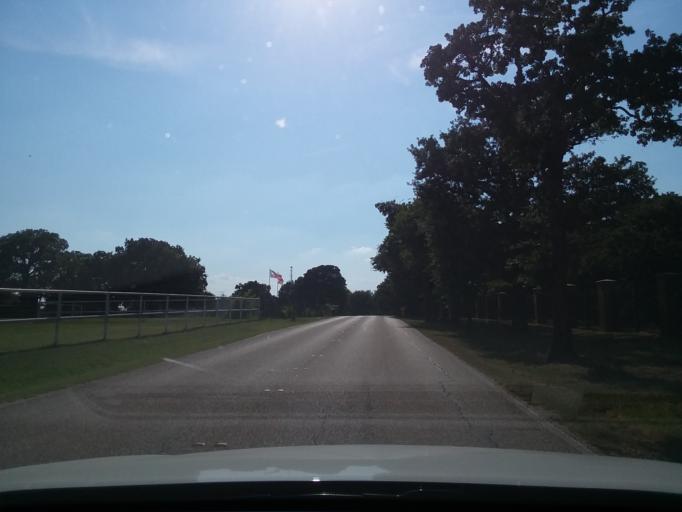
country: US
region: Texas
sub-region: Denton County
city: Bartonville
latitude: 33.0587
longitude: -97.1261
